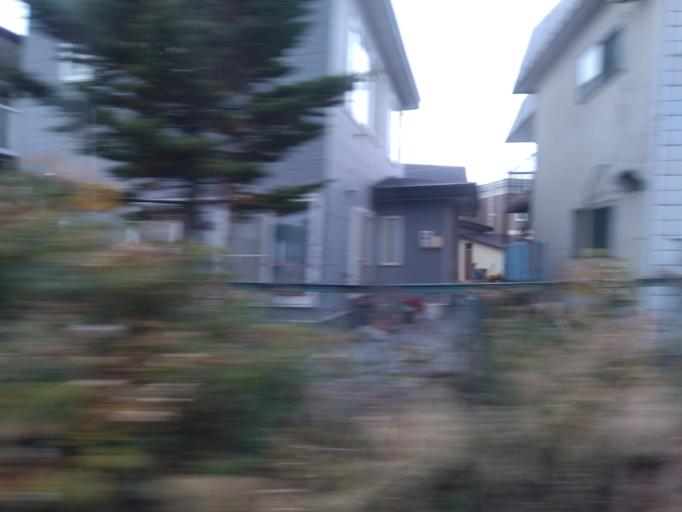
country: JP
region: Hokkaido
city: Hakodate
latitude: 41.8086
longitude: 140.7325
